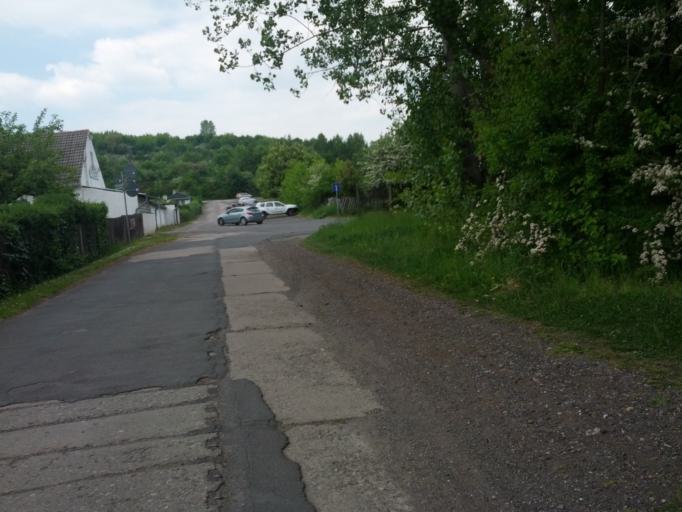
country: DE
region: Thuringia
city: Eisenach
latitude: 50.9947
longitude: 10.3003
